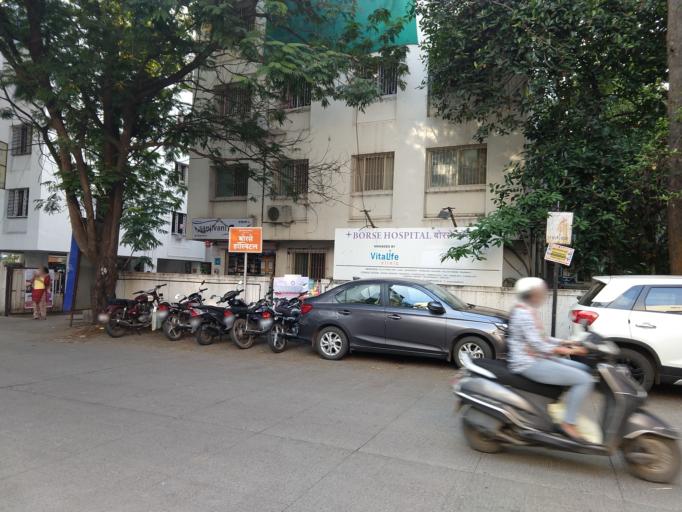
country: IN
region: Maharashtra
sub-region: Pune Division
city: Shivaji Nagar
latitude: 18.5092
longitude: 73.7904
